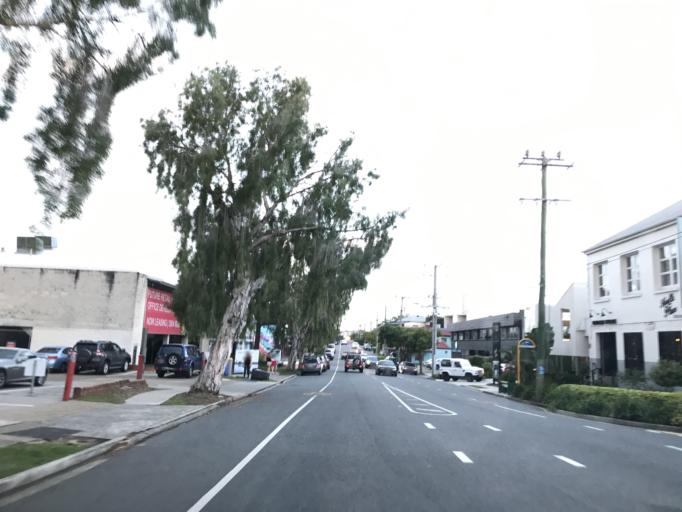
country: AU
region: Queensland
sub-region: Brisbane
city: Toowong
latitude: -27.4860
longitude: 153.0016
